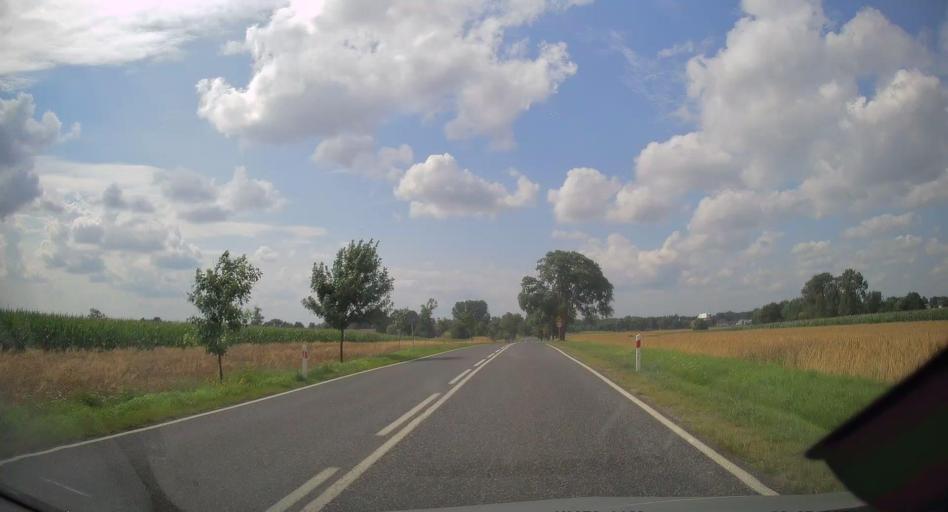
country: PL
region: Lodz Voivodeship
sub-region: Powiat brzezinski
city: Jezow
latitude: 51.8014
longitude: 20.0201
